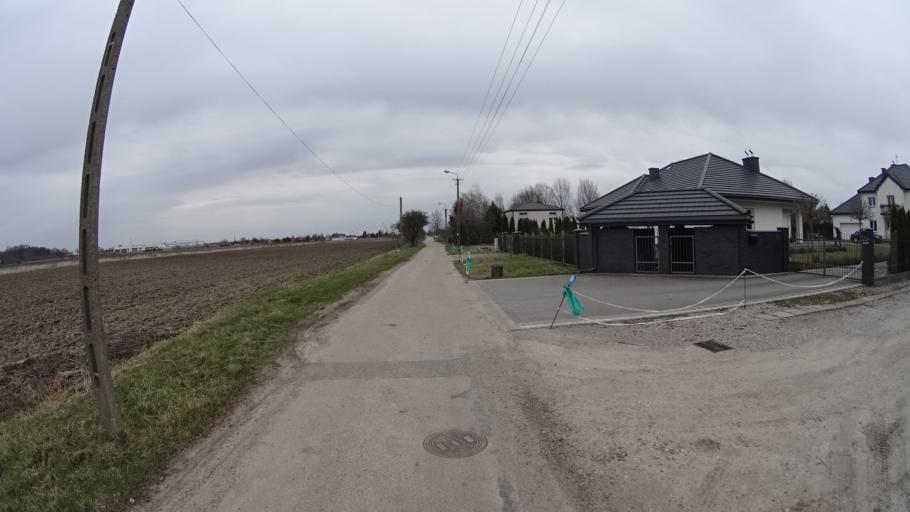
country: PL
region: Masovian Voivodeship
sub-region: Powiat warszawski zachodni
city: Stare Babice
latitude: 52.2441
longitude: 20.8081
